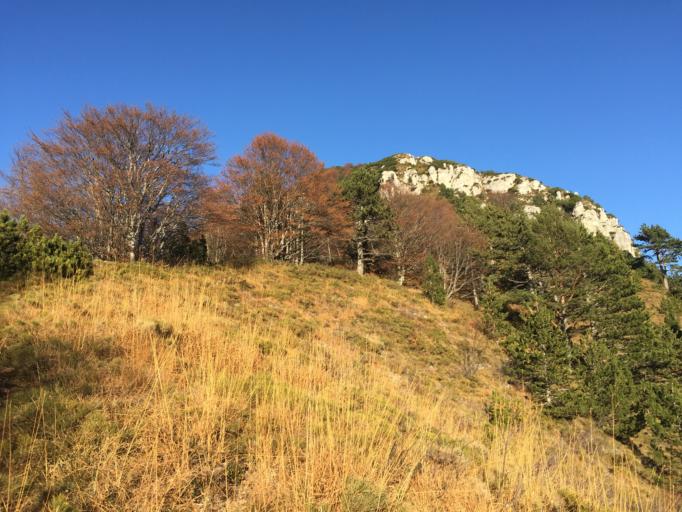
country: IT
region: Friuli Venezia Giulia
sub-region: Provincia di Udine
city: Chiusaforte
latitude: 46.4178
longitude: 13.2832
